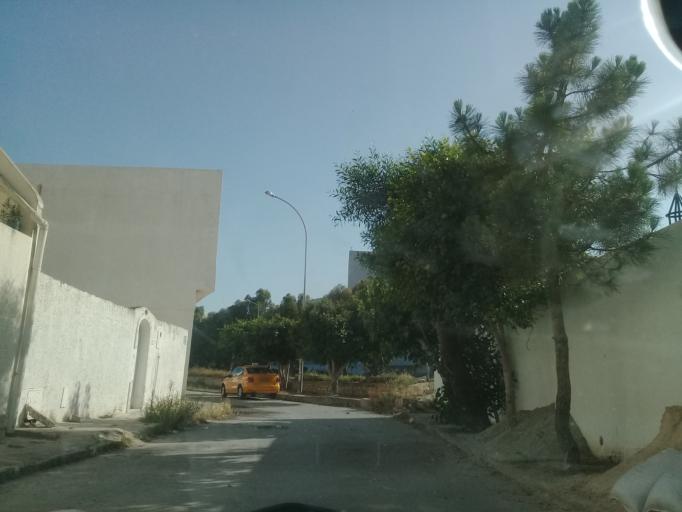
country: TN
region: Ariana
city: Ariana
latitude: 36.8345
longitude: 10.1907
